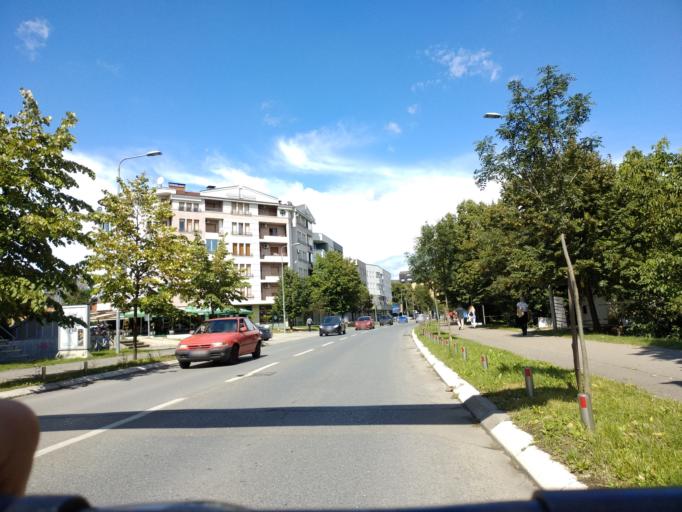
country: BA
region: Republika Srpska
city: Mejdan - Obilicevo
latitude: 44.7683
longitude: 17.1990
